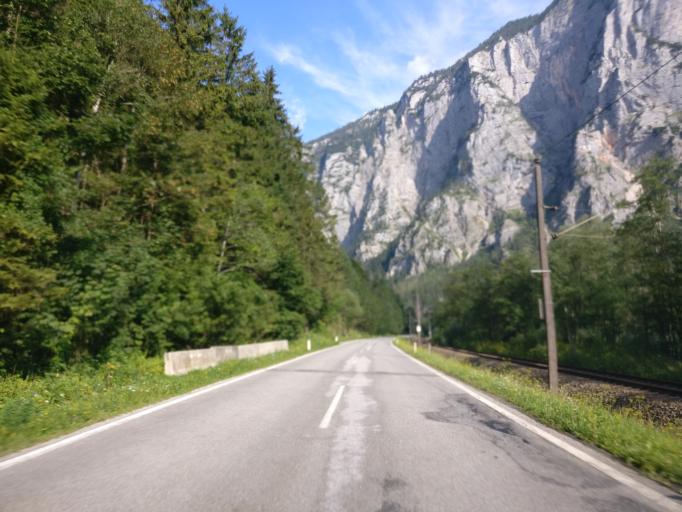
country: AT
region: Styria
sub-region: Politischer Bezirk Leoben
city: Hieflau
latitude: 47.5900
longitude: 14.6590
